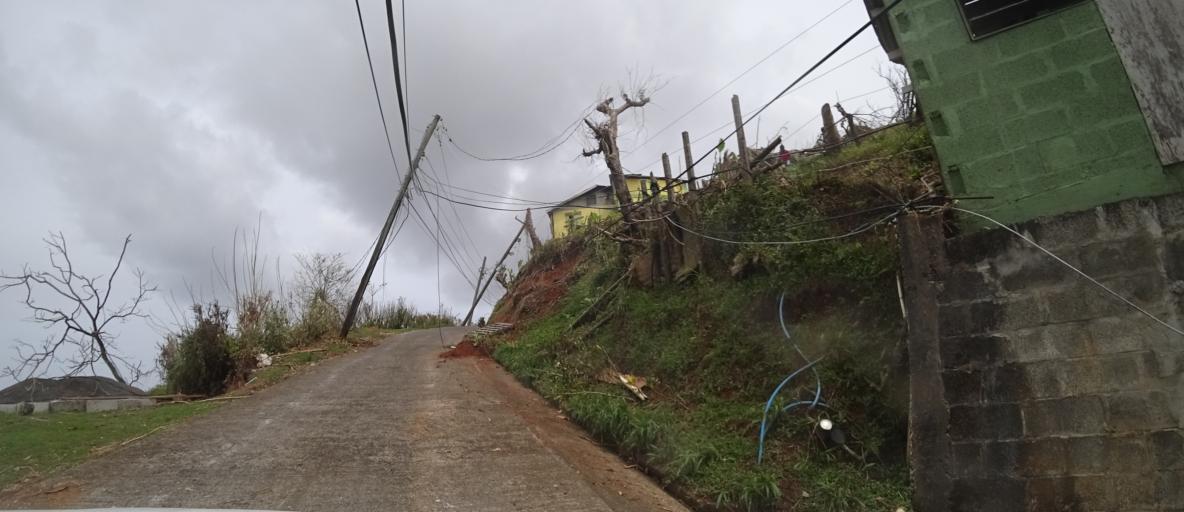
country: DM
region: Saint Andrew
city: Calibishie
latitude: 15.5879
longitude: -61.4055
